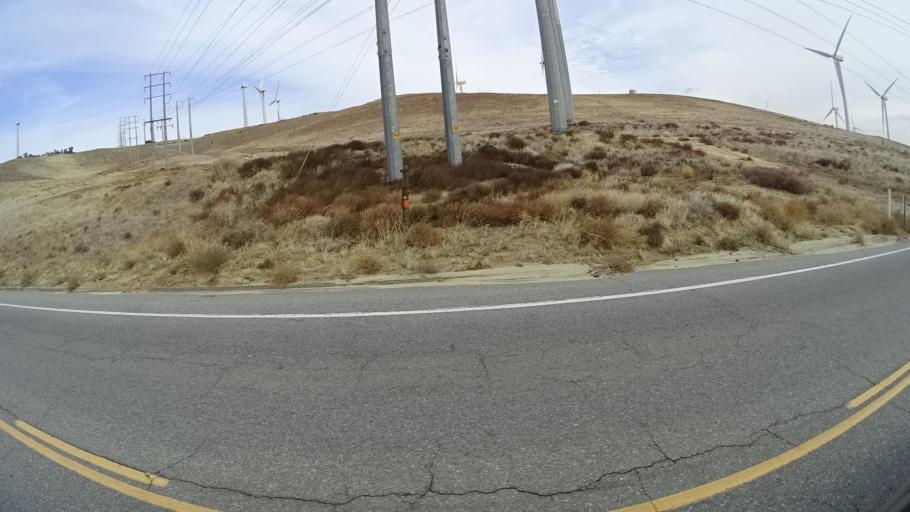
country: US
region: California
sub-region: Kern County
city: Tehachapi
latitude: 35.0539
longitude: -118.3644
